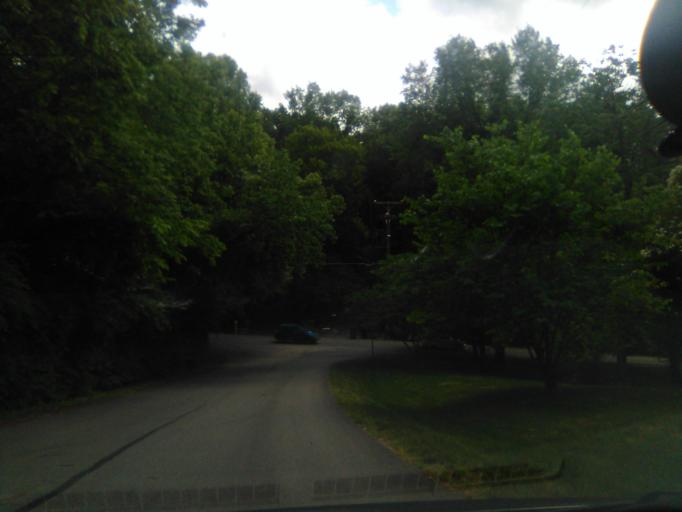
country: US
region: Tennessee
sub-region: Davidson County
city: Belle Meade
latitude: 36.1344
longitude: -86.8724
